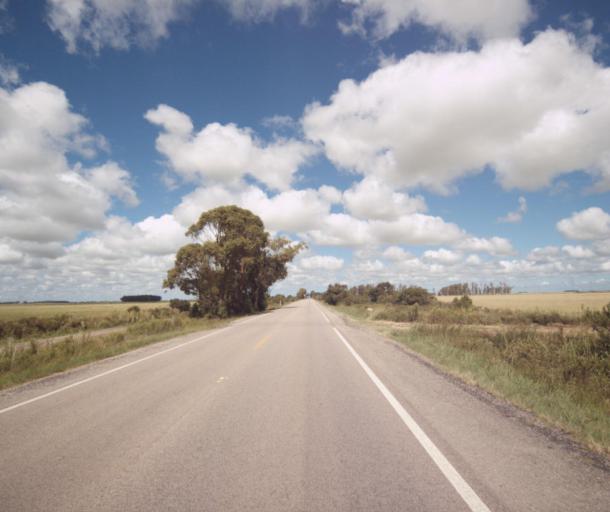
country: BR
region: Rio Grande do Sul
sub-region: Rio Grande
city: Rio Grande
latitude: -32.1777
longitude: -52.4199
